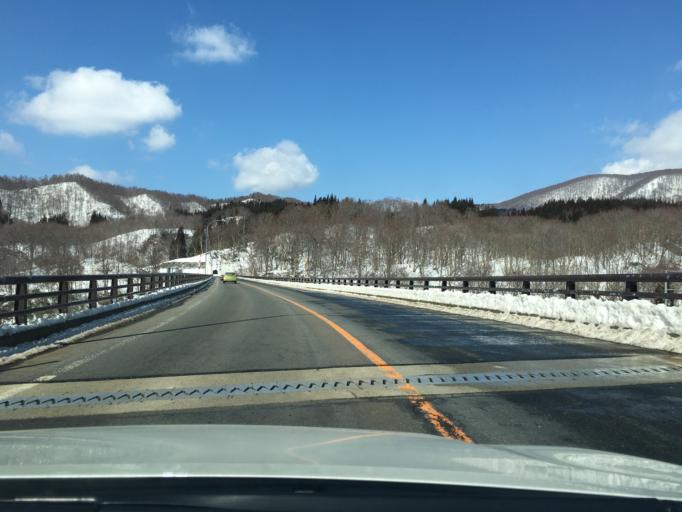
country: JP
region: Yamagata
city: Tsuruoka
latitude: 38.5771
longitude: 139.9435
